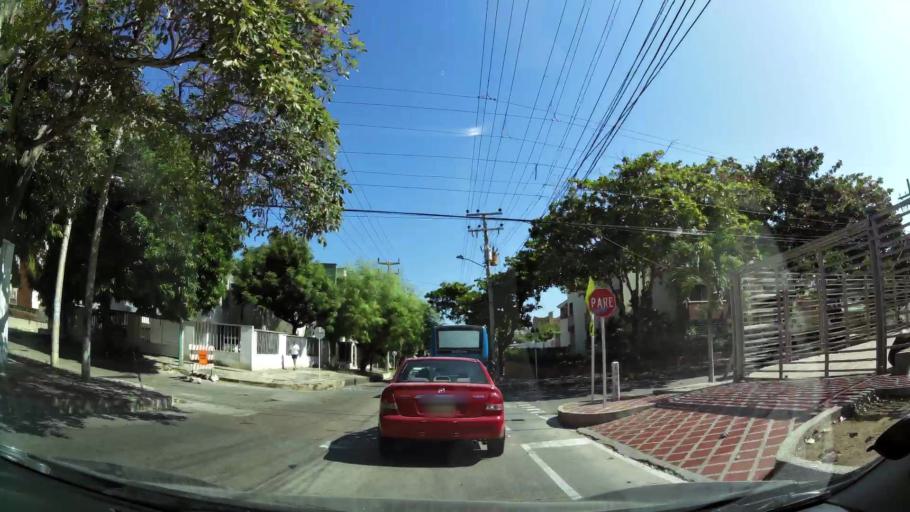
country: CO
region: Atlantico
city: Barranquilla
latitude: 11.0158
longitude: -74.8136
